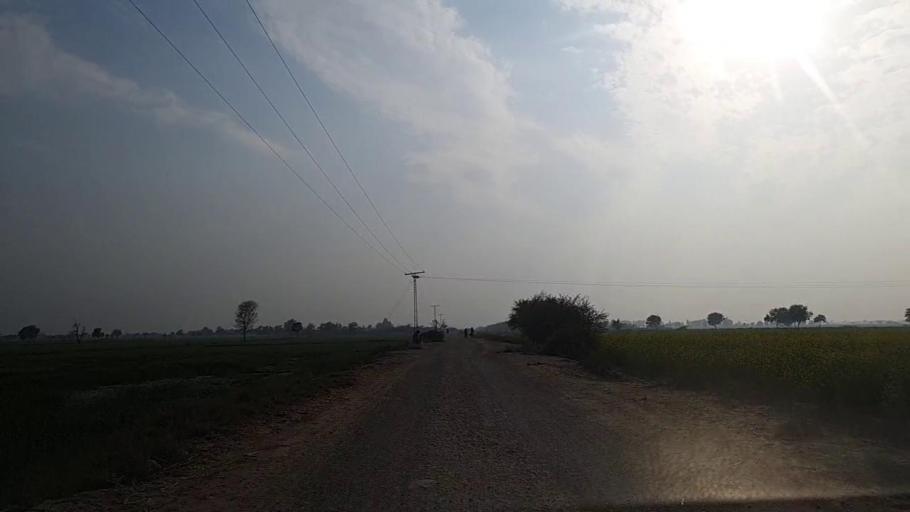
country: PK
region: Sindh
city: Jam Sahib
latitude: 26.3243
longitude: 68.5312
